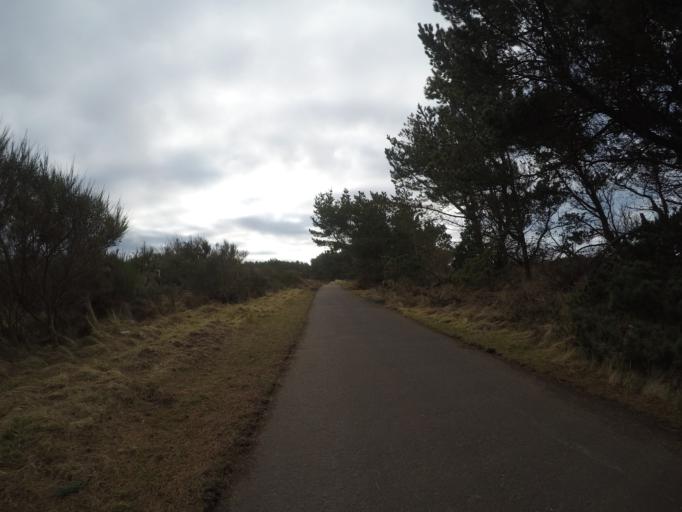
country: GB
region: Scotland
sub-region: North Ayrshire
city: Irvine
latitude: 55.5957
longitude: -4.6741
